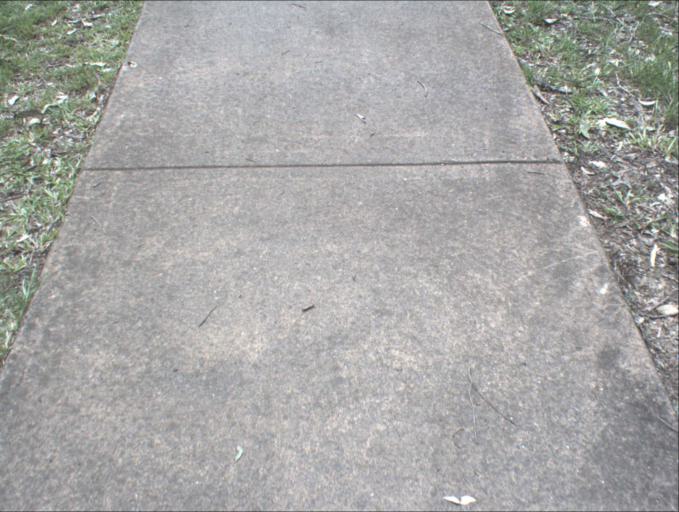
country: AU
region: Queensland
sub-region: Brisbane
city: Forest Lake
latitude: -27.6635
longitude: 152.9975
